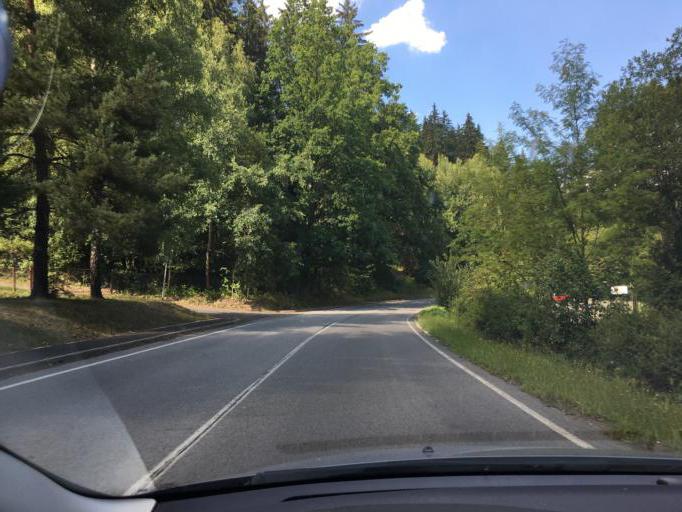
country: CZ
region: Liberecky
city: Semily
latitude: 50.5985
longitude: 15.3544
